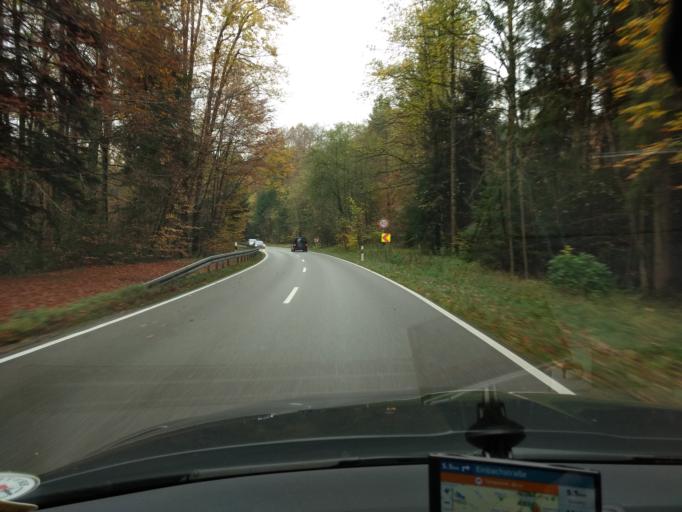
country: DE
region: Bavaria
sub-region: Upper Bavaria
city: Bad Toelz
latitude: 47.8070
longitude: 11.5441
